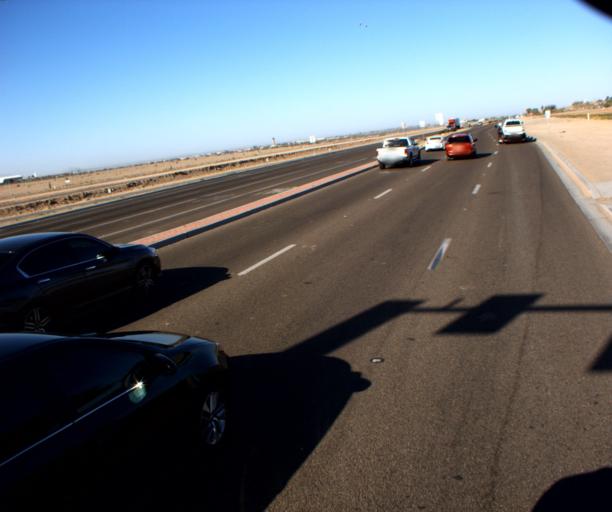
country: US
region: Arizona
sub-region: Yuma County
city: Yuma
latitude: 32.6698
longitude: -114.5819
